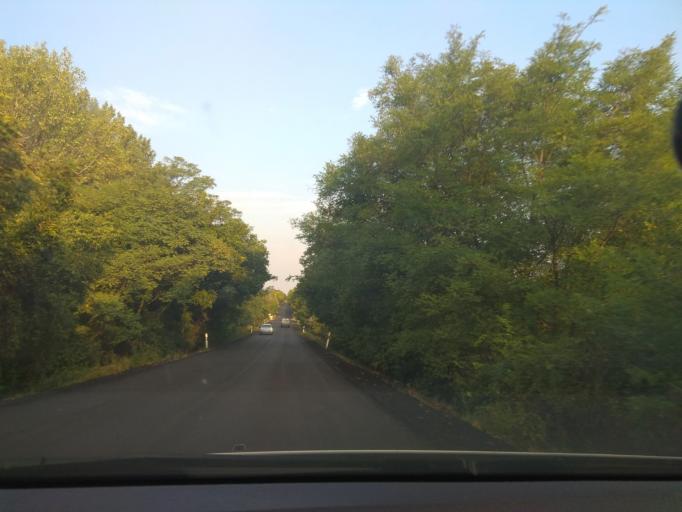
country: HU
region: Heves
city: Szihalom
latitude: 47.8190
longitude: 20.5040
